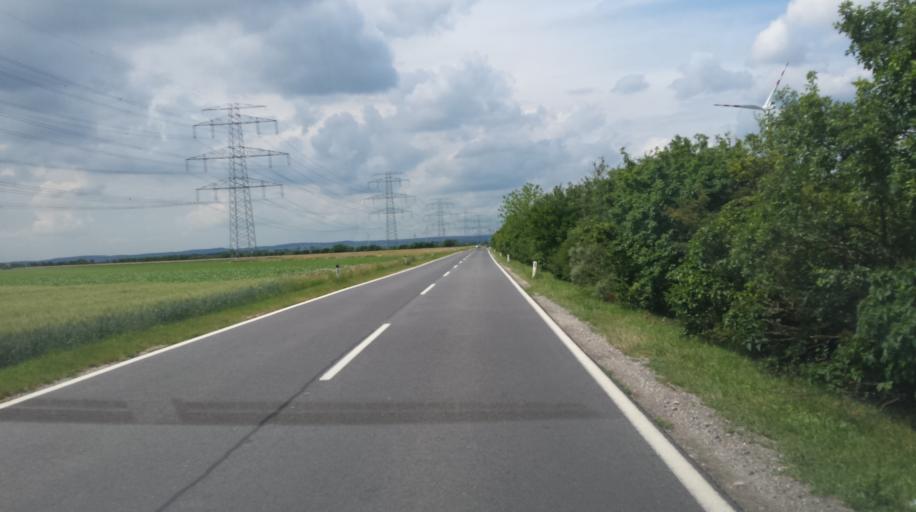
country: AT
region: Lower Austria
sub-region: Politischer Bezirk Ganserndorf
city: Aderklaa
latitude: 48.3079
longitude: 16.5388
